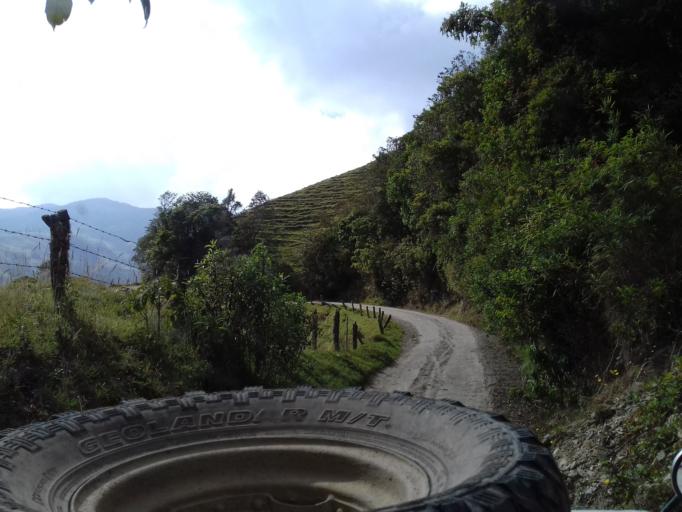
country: CO
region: Quindio
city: Salento
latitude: 4.5483
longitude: -75.4933
